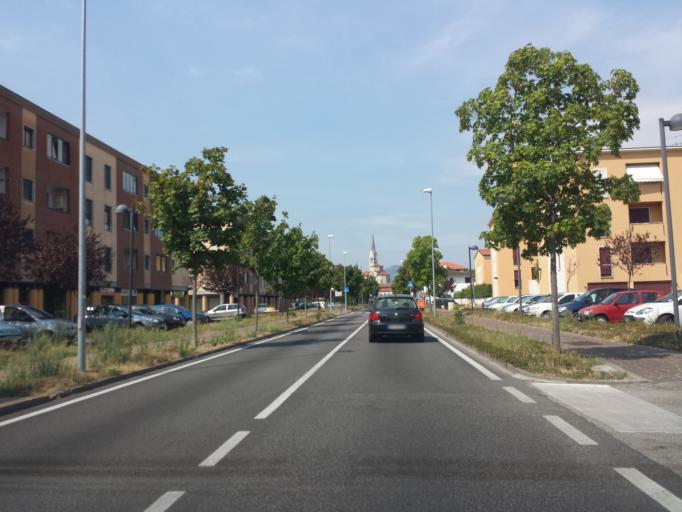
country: IT
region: Veneto
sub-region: Provincia di Vicenza
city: Montecchio Maggiore-Alte Ceccato
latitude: 45.5054
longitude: 11.4168
